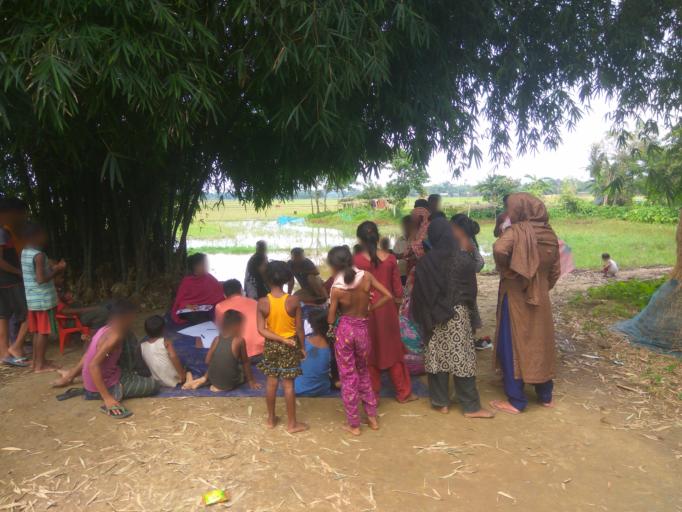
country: IN
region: Assam
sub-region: Karimganj
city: Karimganj
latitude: 24.8231
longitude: 92.2265
